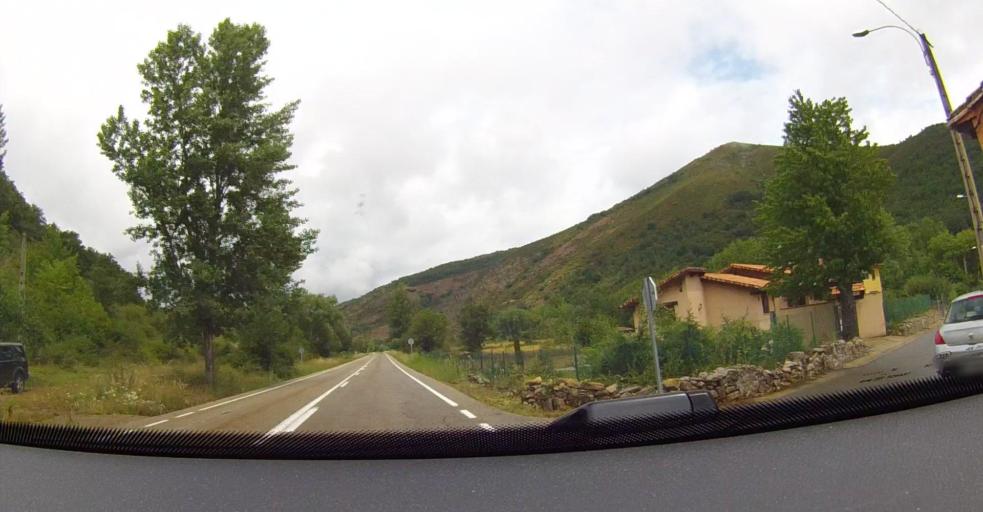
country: ES
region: Castille and Leon
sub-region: Provincia de Leon
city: Bonar
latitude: 42.8870
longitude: -5.3085
